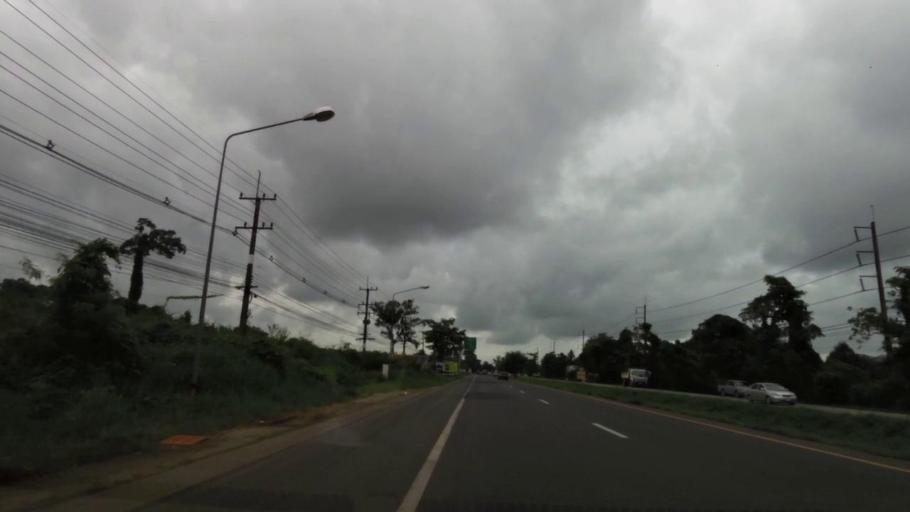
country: TH
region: Chanthaburi
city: Tha Mai
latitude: 12.6644
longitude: 102.0082
